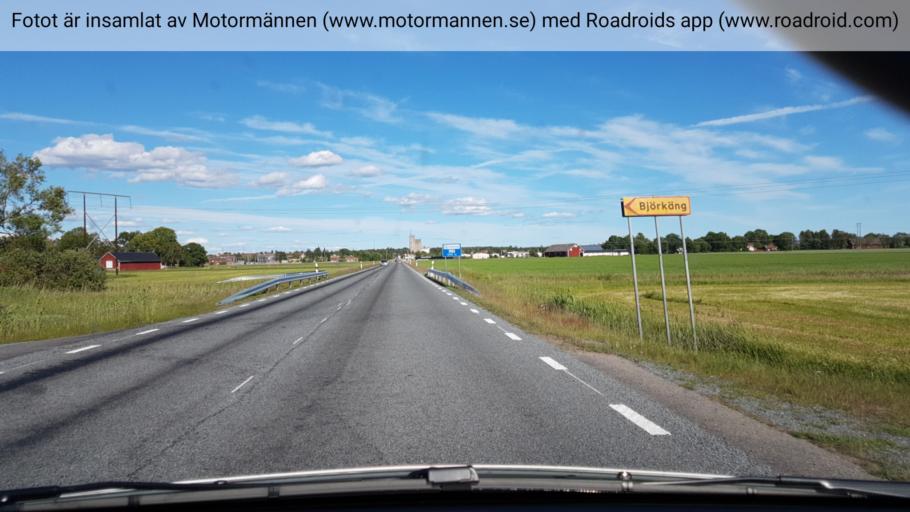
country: SE
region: Vaestra Goetaland
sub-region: Toreboda Kommun
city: Toereboda
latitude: 58.7053
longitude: 14.0991
